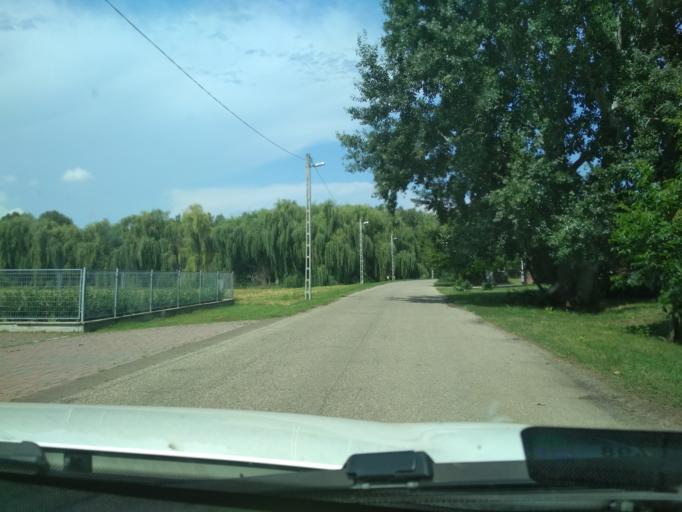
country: HU
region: Jasz-Nagykun-Szolnok
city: Abadszalok
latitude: 47.4764
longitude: 20.5846
